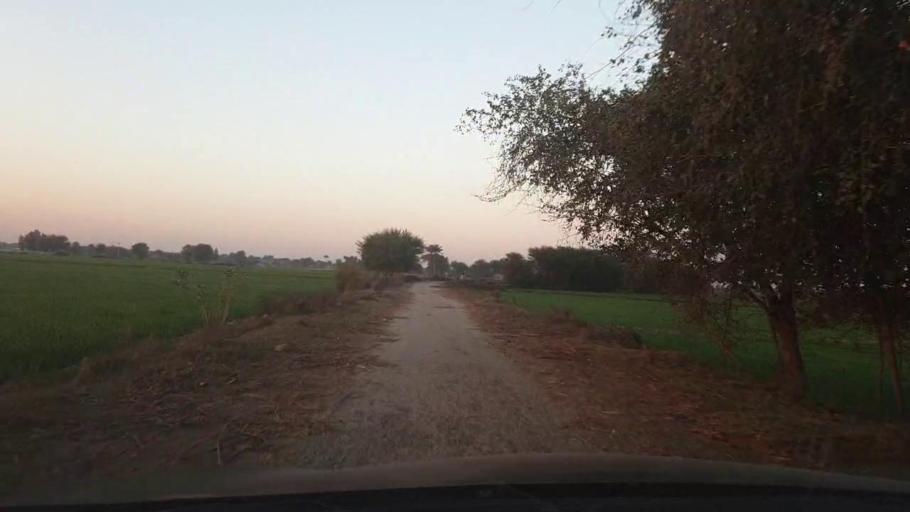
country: PK
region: Sindh
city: Ubauro
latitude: 28.1694
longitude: 69.6354
